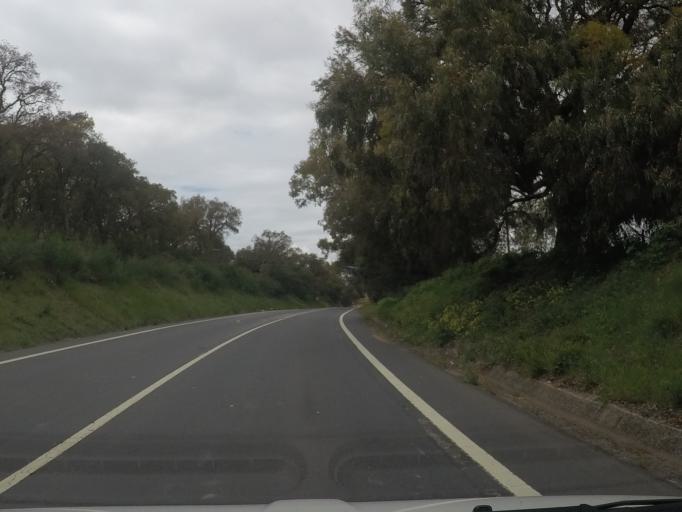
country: PT
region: Setubal
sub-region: Santiago do Cacem
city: Cercal
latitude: 37.8325
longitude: -8.7023
